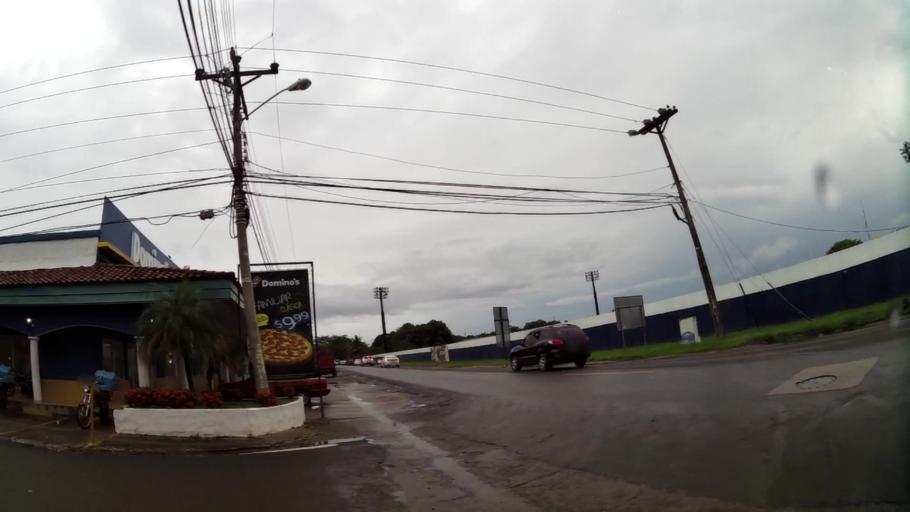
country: PA
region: Veraguas
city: Santiago de Veraguas
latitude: 8.1090
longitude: -80.9737
